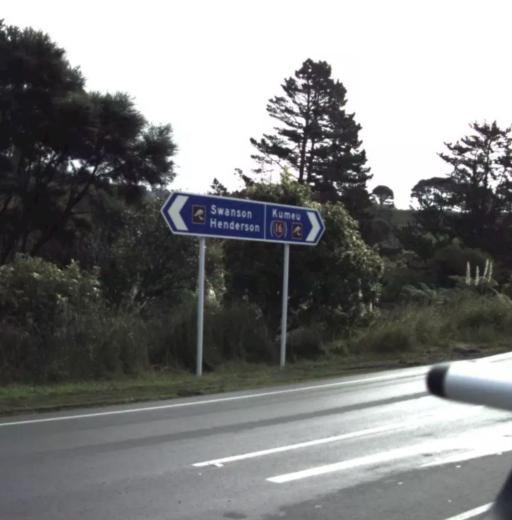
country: NZ
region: Auckland
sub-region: Auckland
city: Muriwai Beach
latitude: -36.8516
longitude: 174.5437
